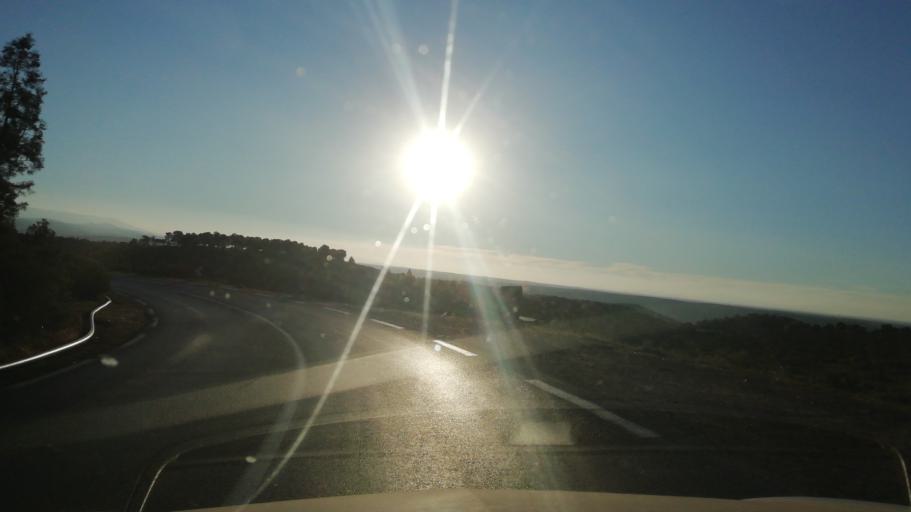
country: DZ
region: Tlemcen
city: Beni Mester
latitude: 34.8143
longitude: -1.6207
